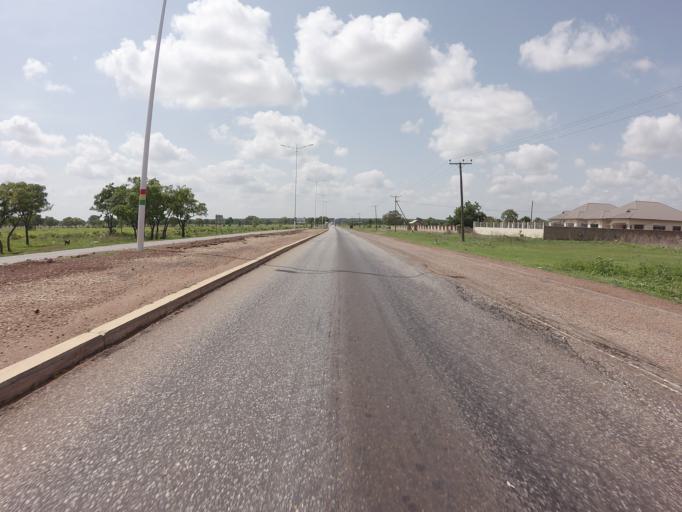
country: GH
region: Northern
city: Savelugu
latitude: 9.5546
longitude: -0.8371
